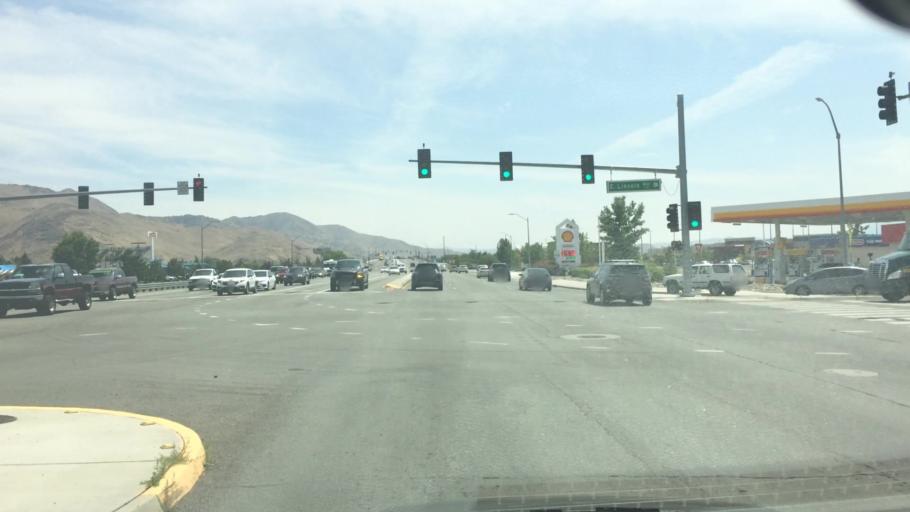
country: US
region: Nevada
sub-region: Washoe County
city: Sparks
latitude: 39.5339
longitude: -119.7155
